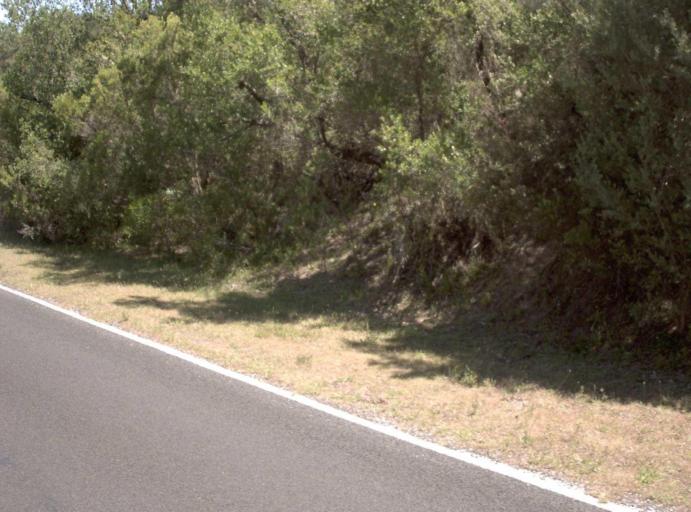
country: AU
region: Victoria
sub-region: Latrobe
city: Morwell
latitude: -38.8843
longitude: 146.2582
